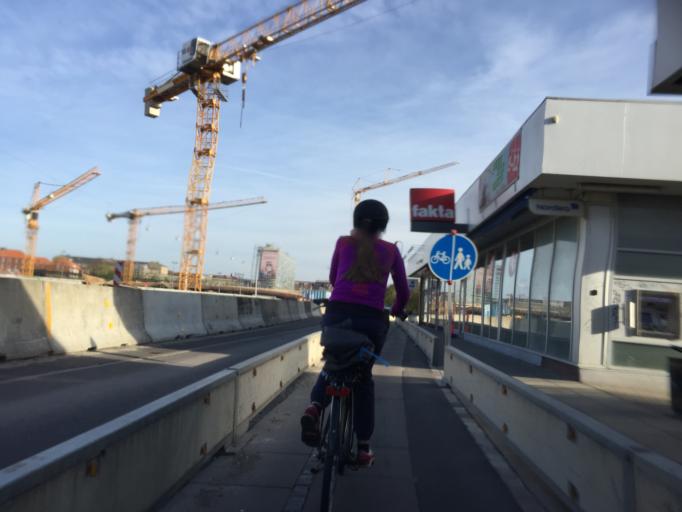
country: DK
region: Capital Region
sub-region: Kobenhavn
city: Copenhagen
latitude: 55.7181
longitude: 12.5567
